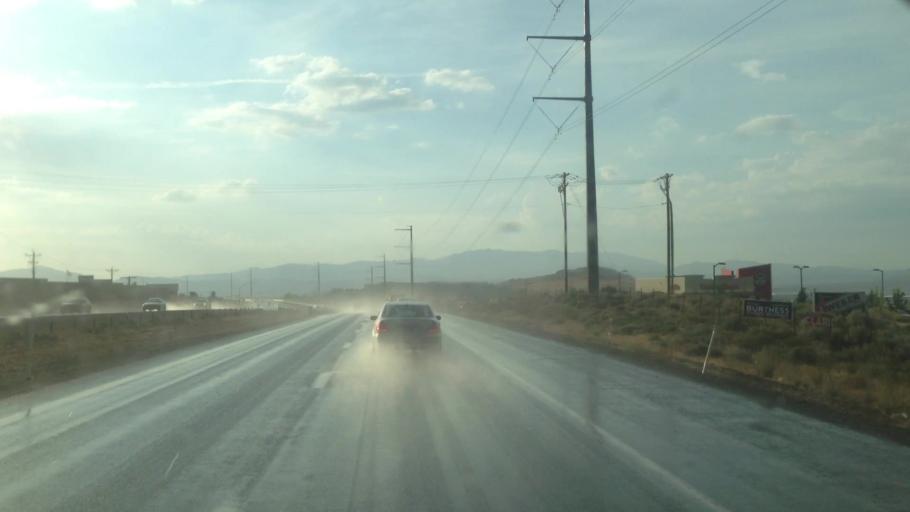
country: US
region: Nevada
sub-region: Washoe County
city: Golden Valley
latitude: 39.6057
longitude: -119.8434
